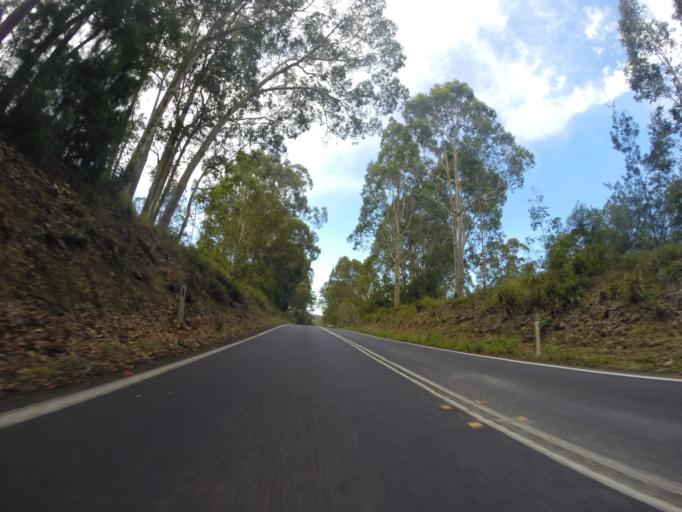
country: AU
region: New South Wales
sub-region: Shoalhaven Shire
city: Falls Creek
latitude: -35.0852
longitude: 150.5164
